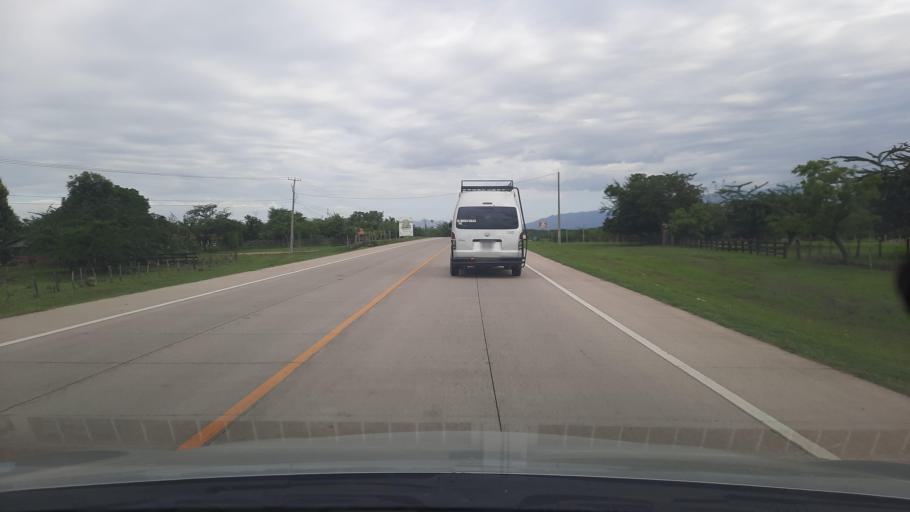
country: NI
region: Chinandega
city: Somotillo
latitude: 12.8847
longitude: -86.8502
